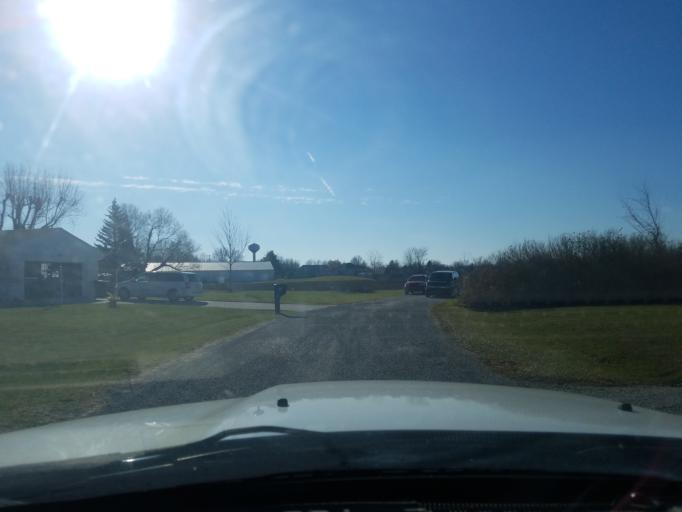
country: US
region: Indiana
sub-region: Wells County
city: Ossian
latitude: 40.8898
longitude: -85.1678
